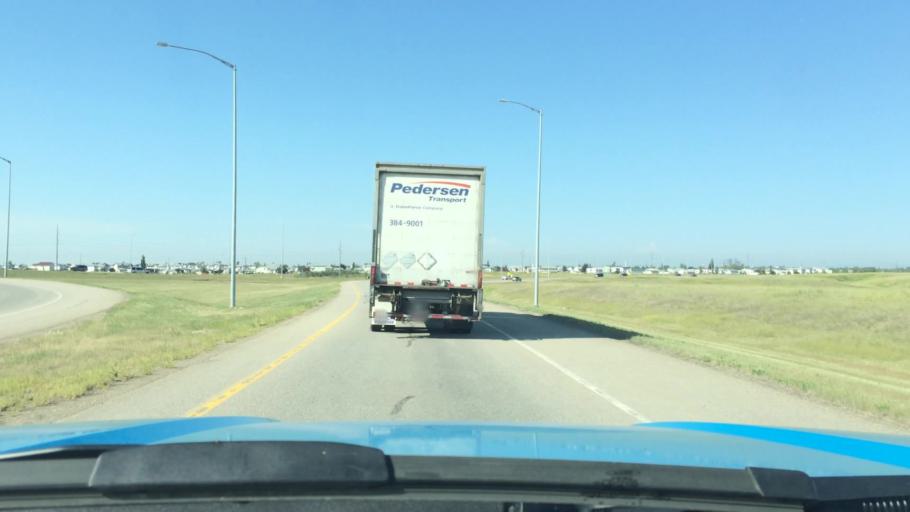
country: CA
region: Alberta
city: Chestermere
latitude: 51.0985
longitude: -113.9218
